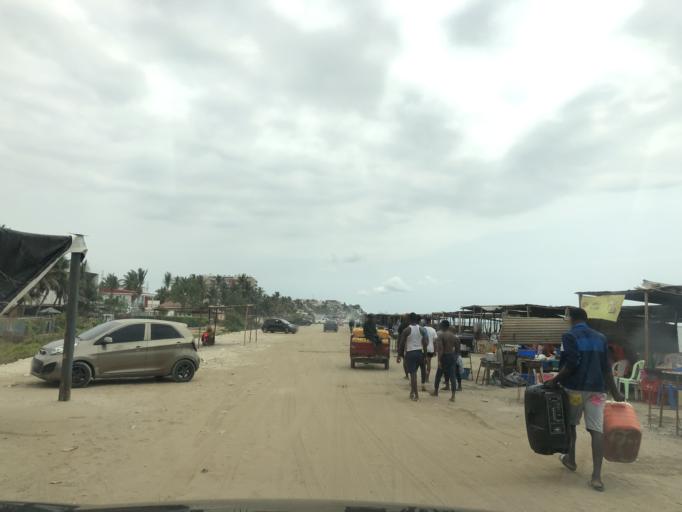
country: AO
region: Luanda
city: Luanda
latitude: -8.8733
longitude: 13.1926
